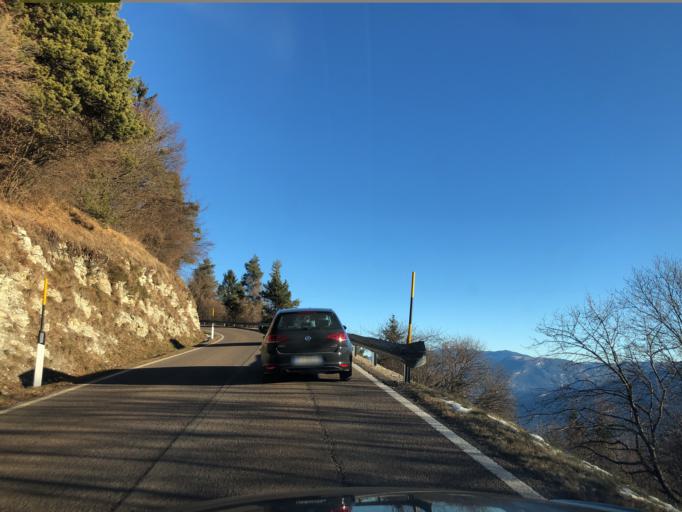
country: IT
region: Trentino-Alto Adige
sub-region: Provincia di Trento
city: Brentonico
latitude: 45.7979
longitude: 10.9279
